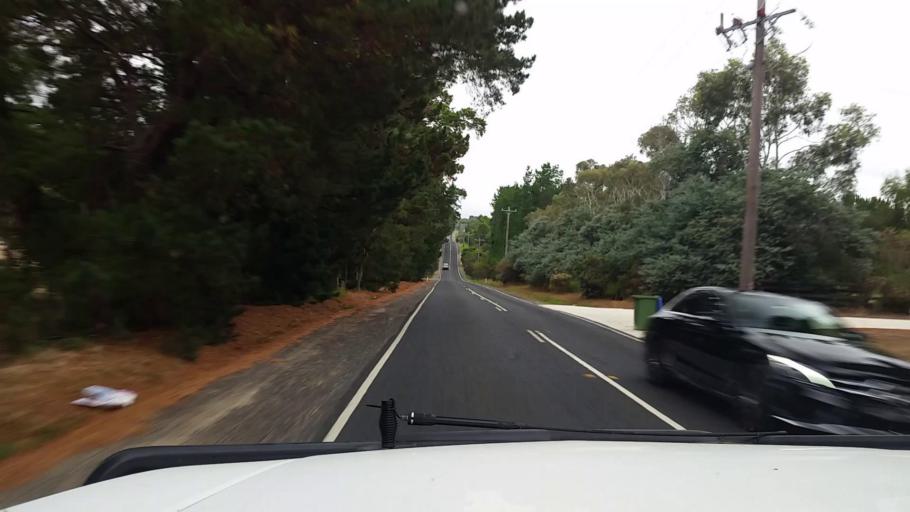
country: AU
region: Victoria
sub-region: Mornington Peninsula
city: Hastings
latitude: -38.2976
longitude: 145.1457
